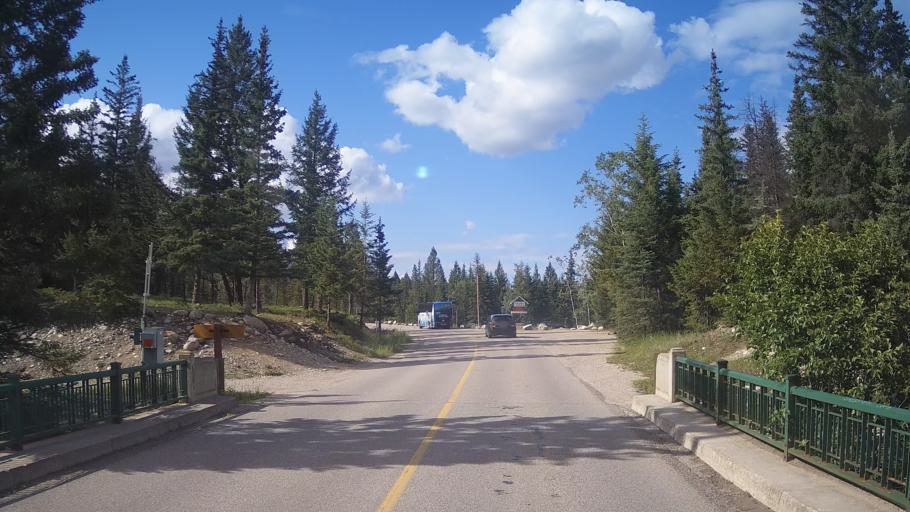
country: CA
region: Alberta
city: Jasper Park Lodge
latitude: 52.8656
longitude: -118.0706
